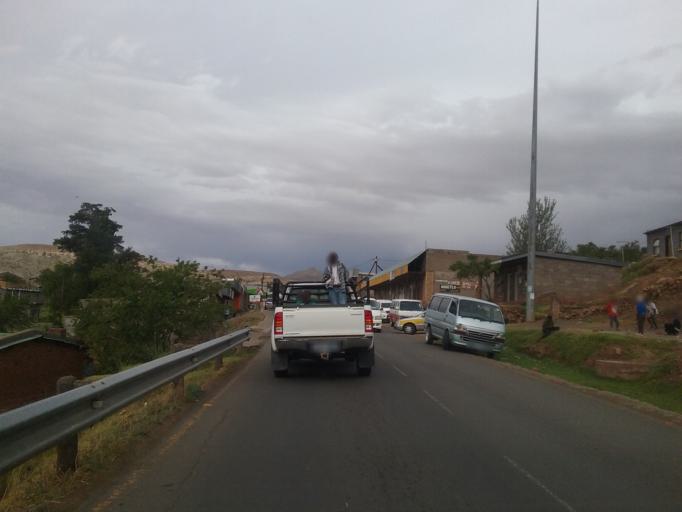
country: LS
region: Quthing
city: Quthing
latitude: -30.4005
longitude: 27.6978
